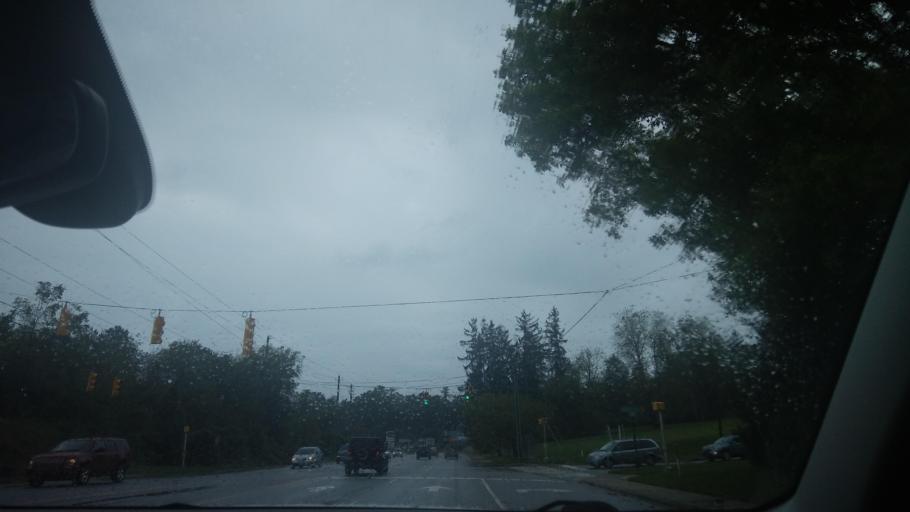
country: US
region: North Carolina
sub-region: Buncombe County
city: Biltmore Forest
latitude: 35.5558
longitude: -82.5384
